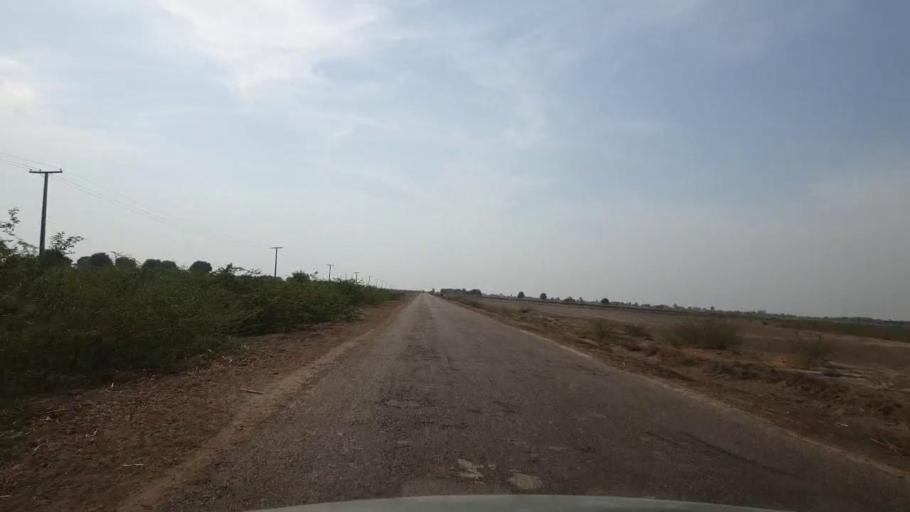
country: PK
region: Sindh
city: Kunri
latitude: 25.1585
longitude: 69.4945
